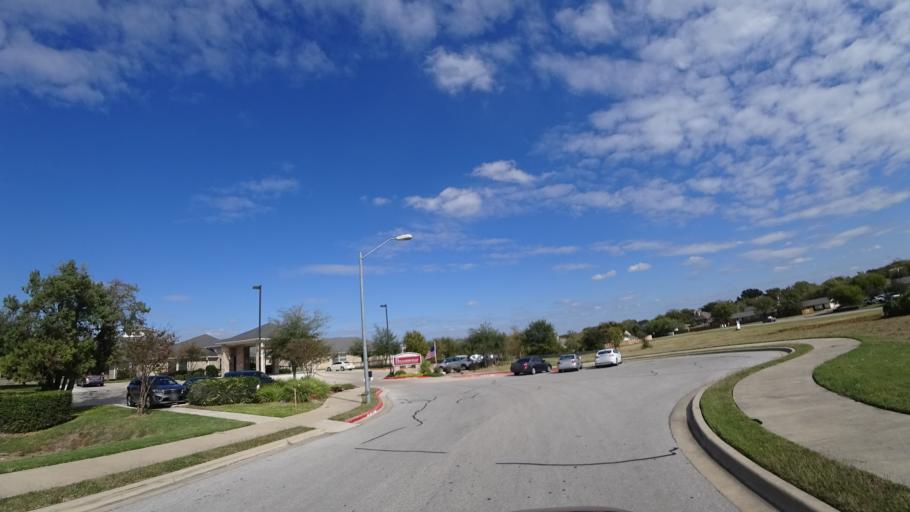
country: US
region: Texas
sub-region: Travis County
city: Pflugerville
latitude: 30.4440
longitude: -97.6283
